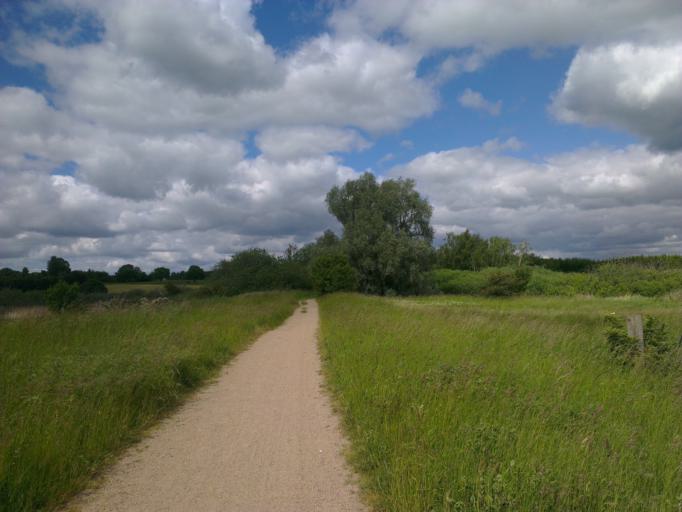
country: DK
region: Capital Region
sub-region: Frederikssund Kommune
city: Slangerup
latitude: 55.8495
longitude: 12.1905
